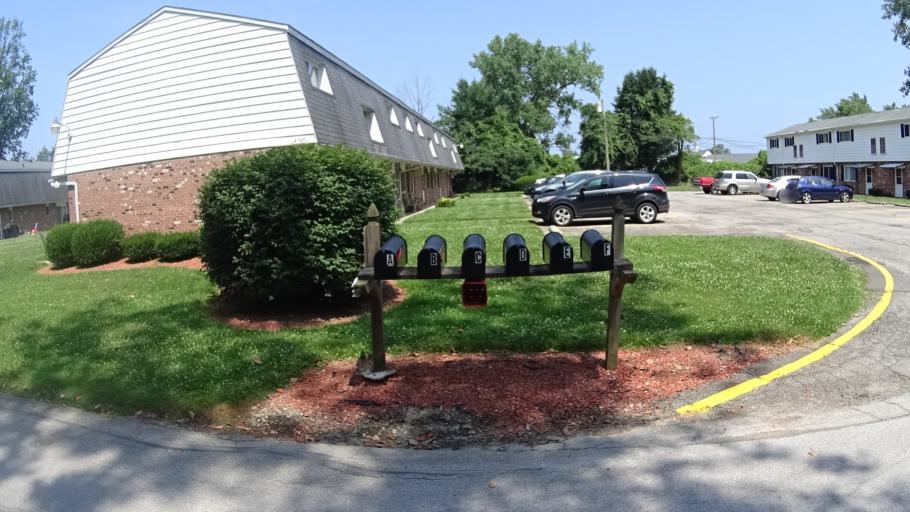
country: US
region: Ohio
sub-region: Lorain County
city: Vermilion
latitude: 41.4222
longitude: -82.3501
